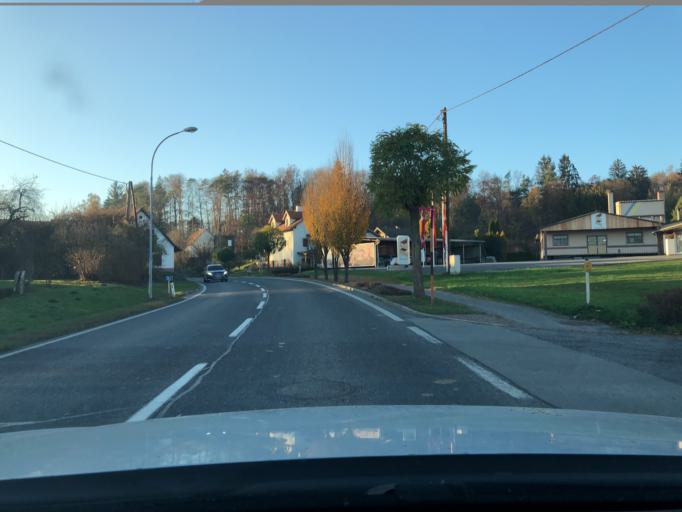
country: AT
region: Styria
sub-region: Politischer Bezirk Weiz
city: Sinabelkirchen
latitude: 47.0989
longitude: 15.8435
